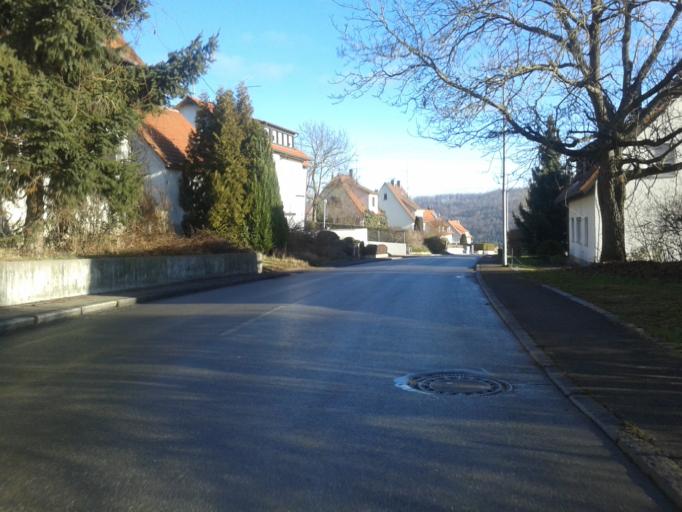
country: DE
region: Baden-Wuerttemberg
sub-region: Tuebingen Region
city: Erbach
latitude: 48.3972
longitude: 9.8618
